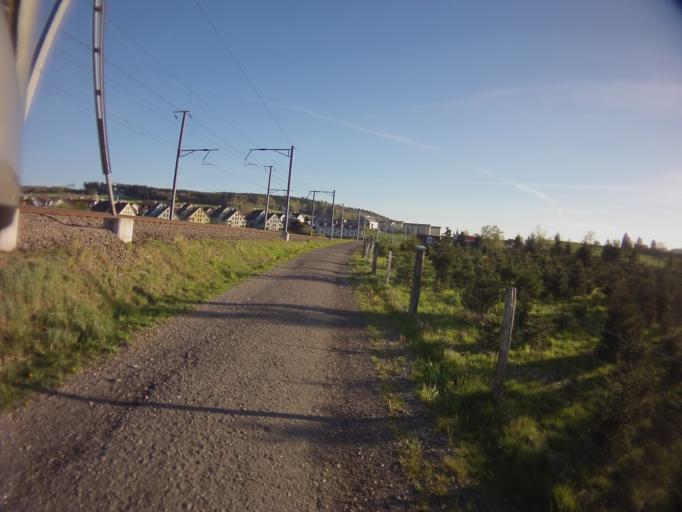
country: CH
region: Zurich
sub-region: Bezirk Affoltern
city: Bonstetten
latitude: 47.3198
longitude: 8.4662
